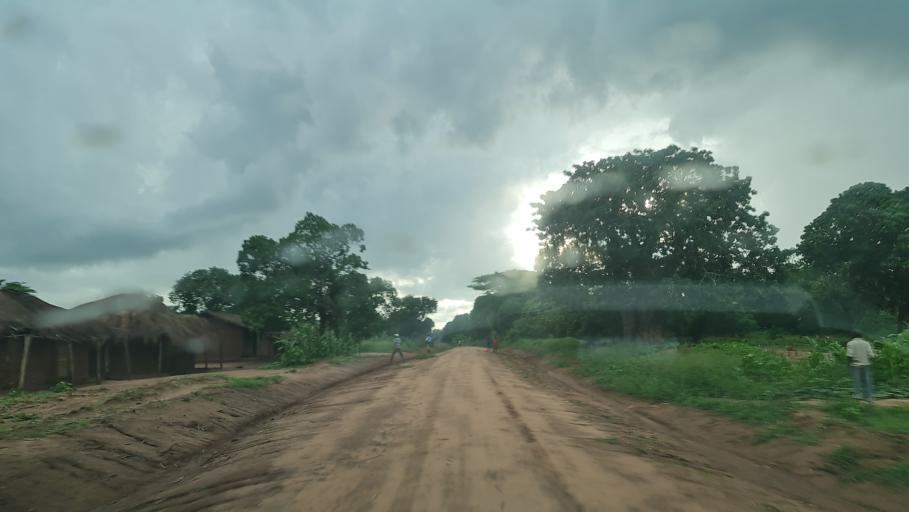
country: MZ
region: Nampula
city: Nacala
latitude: -13.9890
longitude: 40.3752
